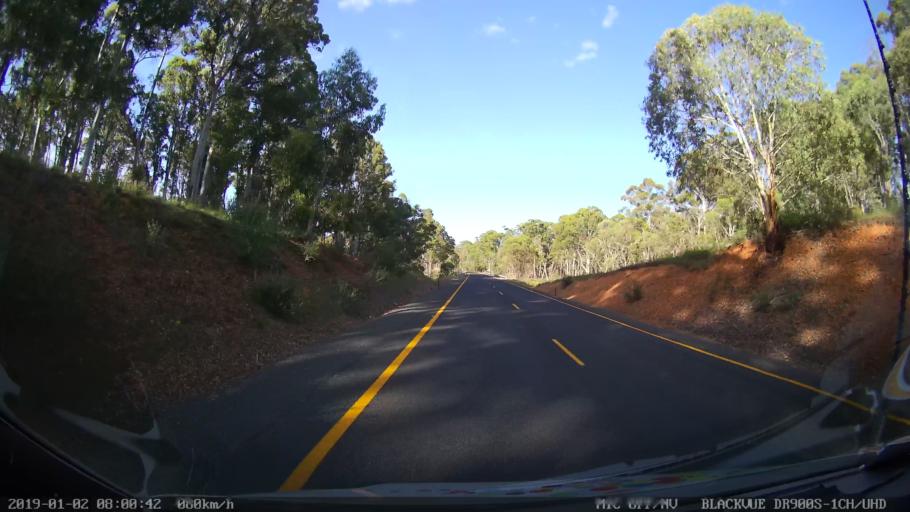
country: AU
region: New South Wales
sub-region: Tumut Shire
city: Tumut
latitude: -35.6455
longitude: 148.4416
